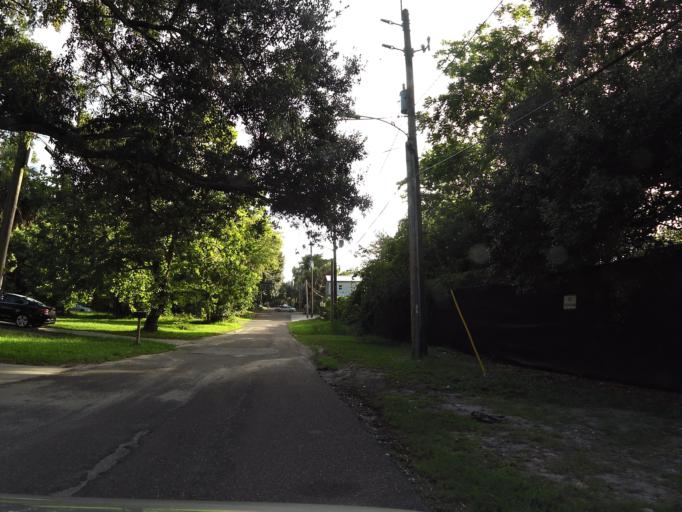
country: US
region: Florida
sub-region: Duval County
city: Jacksonville
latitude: 30.3800
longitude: -81.6667
